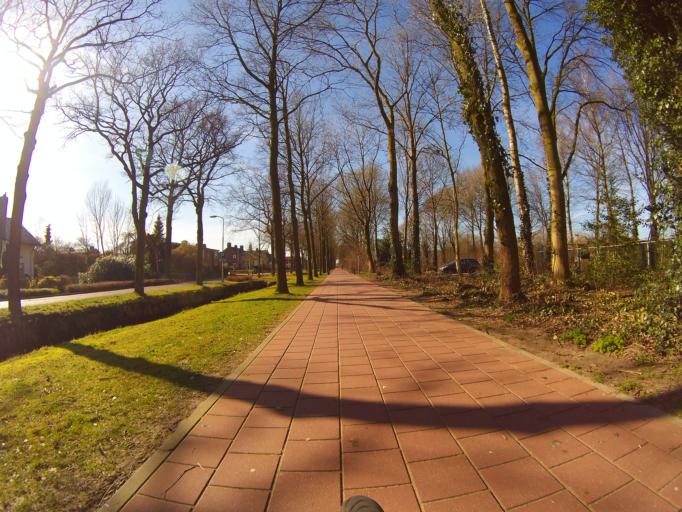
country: NL
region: Utrecht
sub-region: Gemeente Utrechtse Heuvelrug
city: Overberg
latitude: 52.0830
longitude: 5.4891
